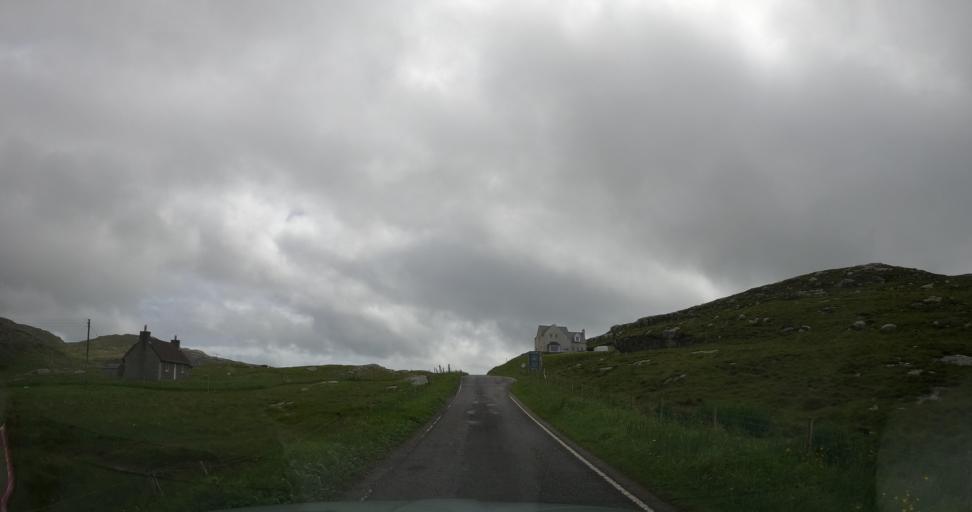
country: GB
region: Scotland
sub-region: Eilean Siar
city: Barra
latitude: 56.9632
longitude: -7.5093
